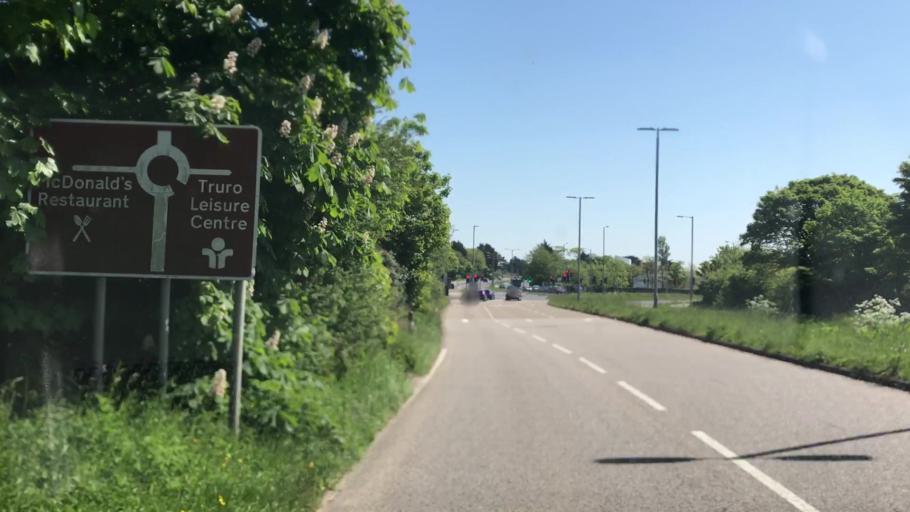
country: GB
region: England
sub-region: Cornwall
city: Truro
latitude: 50.2638
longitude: -5.1049
